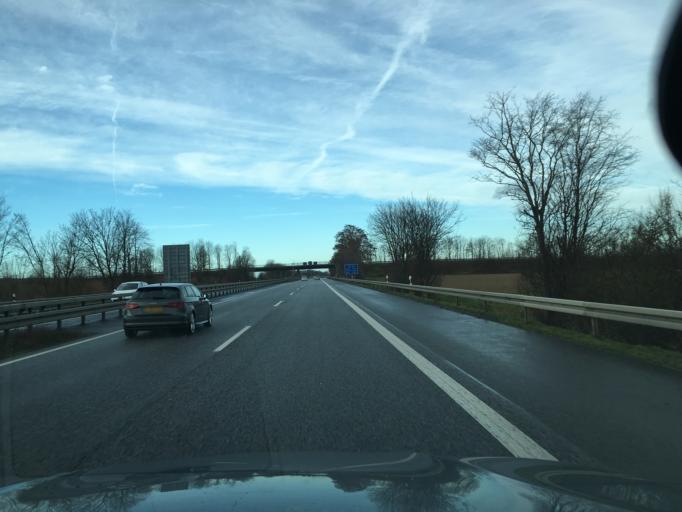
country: DE
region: North Rhine-Westphalia
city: Meckenheim
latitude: 50.5974
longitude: 7.0188
